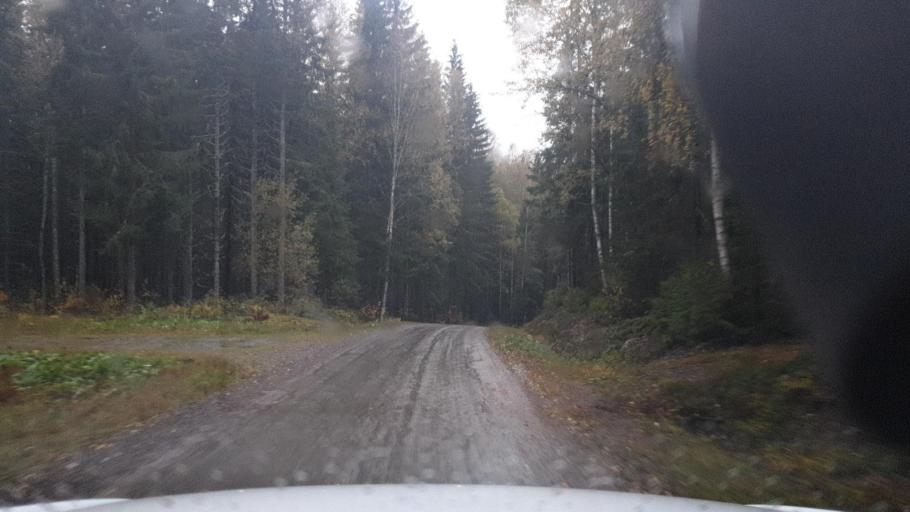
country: SE
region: Vaermland
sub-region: Eda Kommun
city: Amotfors
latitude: 59.8004
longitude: 12.4426
